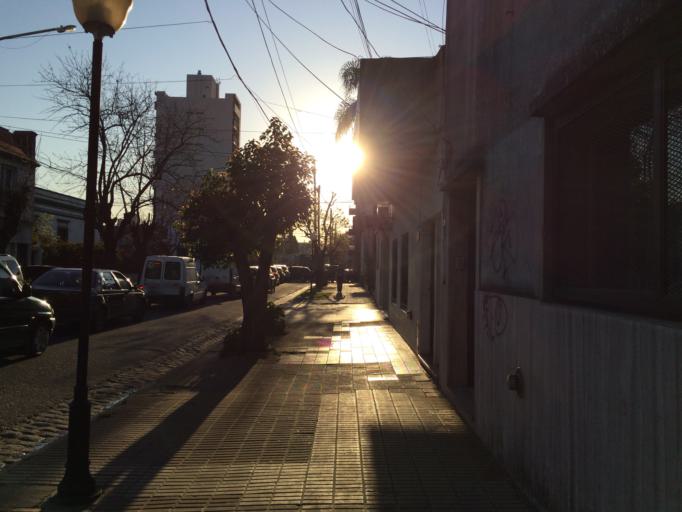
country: AR
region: Buenos Aires
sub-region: Partido de Lomas de Zamora
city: Lomas de Zamora
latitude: -34.7408
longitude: -58.3934
